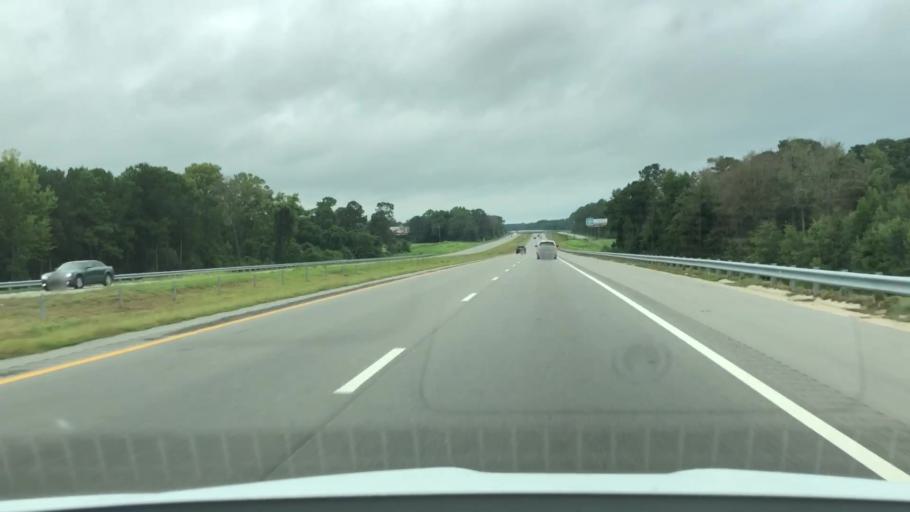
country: US
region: North Carolina
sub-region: Wayne County
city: Elroy
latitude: 35.3441
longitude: -77.8457
